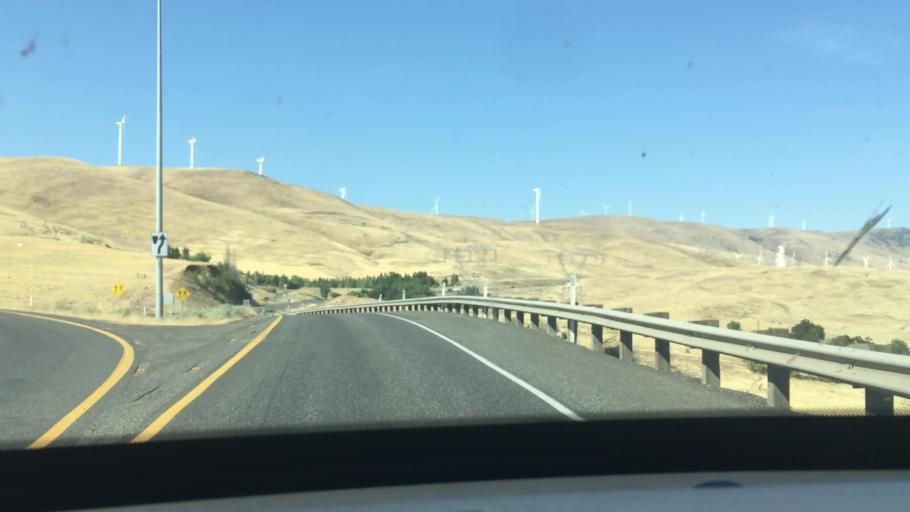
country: US
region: Washington
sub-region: Klickitat County
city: Goldendale
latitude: 45.6981
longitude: -120.8245
